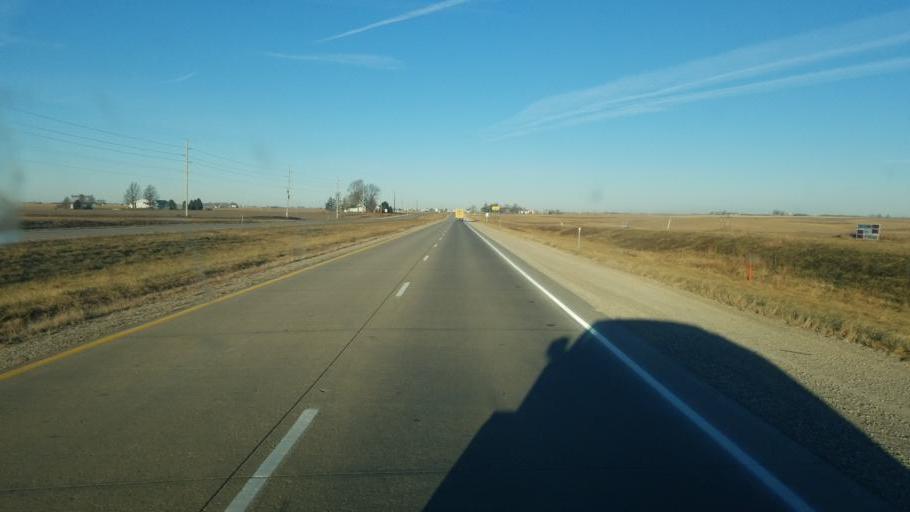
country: US
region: Iowa
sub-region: Marion County
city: Pella
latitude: 41.3612
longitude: -92.7783
